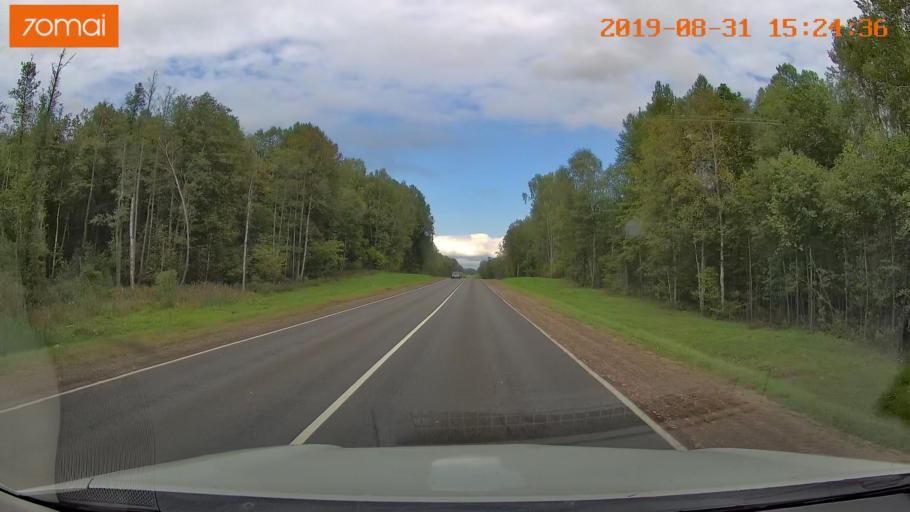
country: RU
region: Kaluga
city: Baryatino
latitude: 54.5300
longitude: 34.5072
